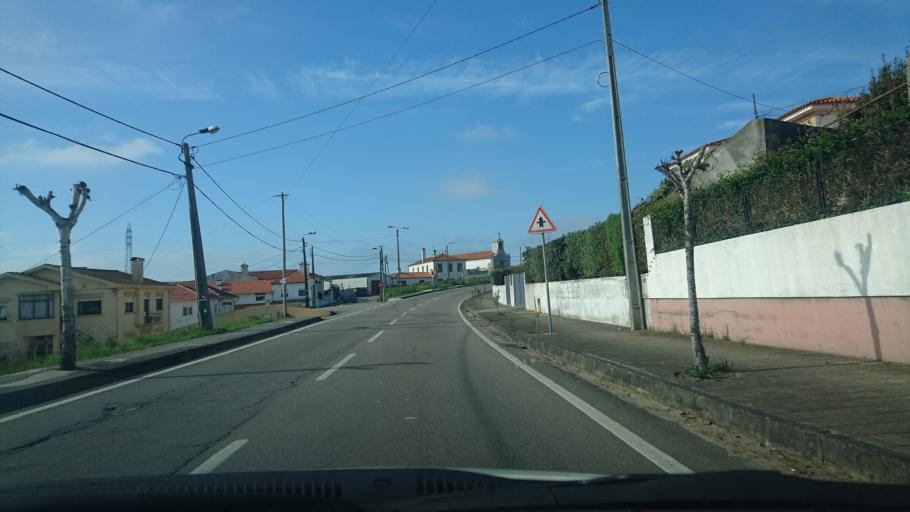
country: PT
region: Aveiro
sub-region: Espinho
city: Souto
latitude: 40.9771
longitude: -8.6310
